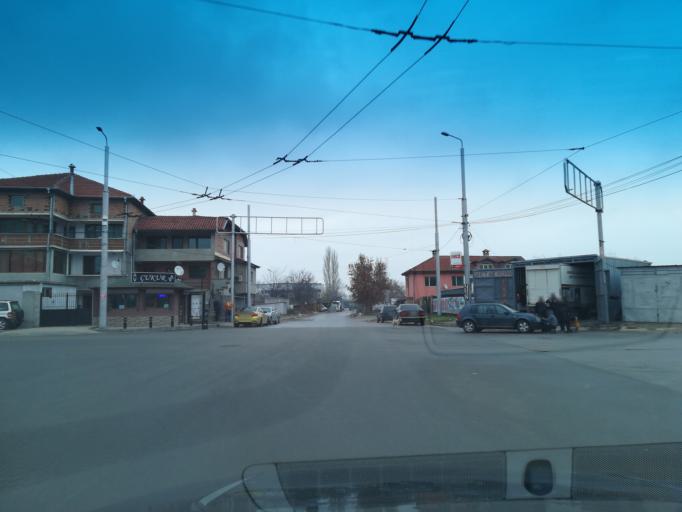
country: BG
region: Plovdiv
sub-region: Obshtina Plovdiv
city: Plovdiv
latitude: 42.1588
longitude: 24.7894
